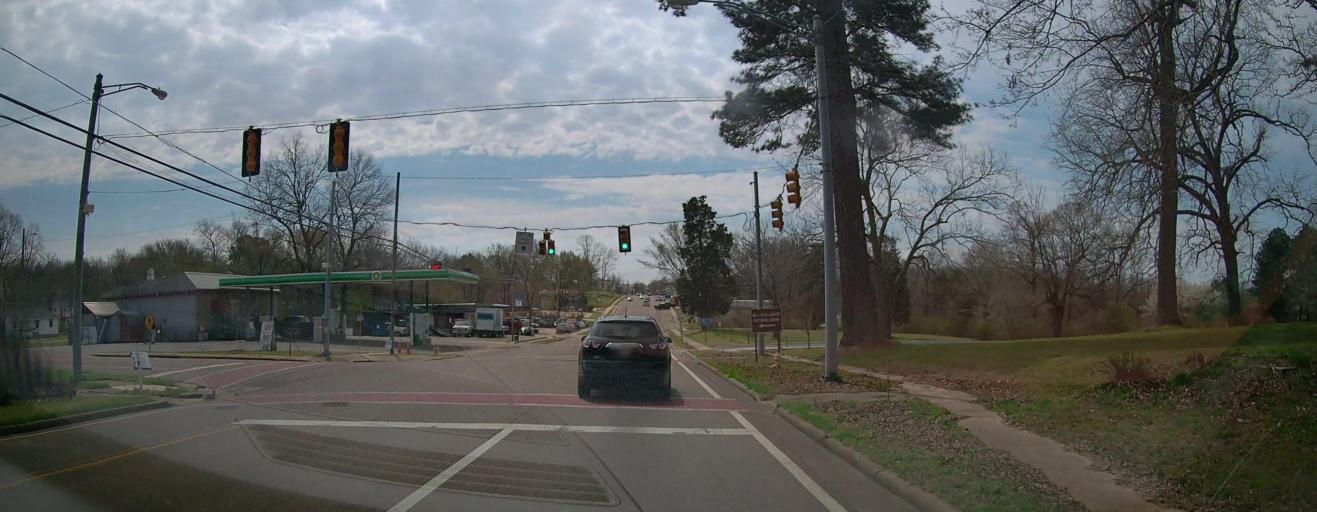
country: US
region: Mississippi
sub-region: Marshall County
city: Holly Springs
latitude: 34.7745
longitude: -89.4485
